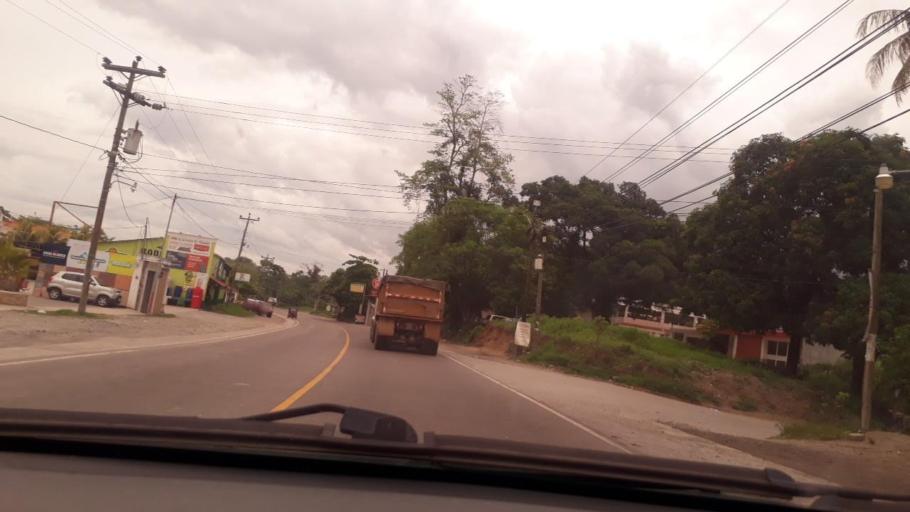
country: GT
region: Izabal
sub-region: Municipio de Los Amates
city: Los Amates
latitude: 15.2567
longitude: -89.0921
